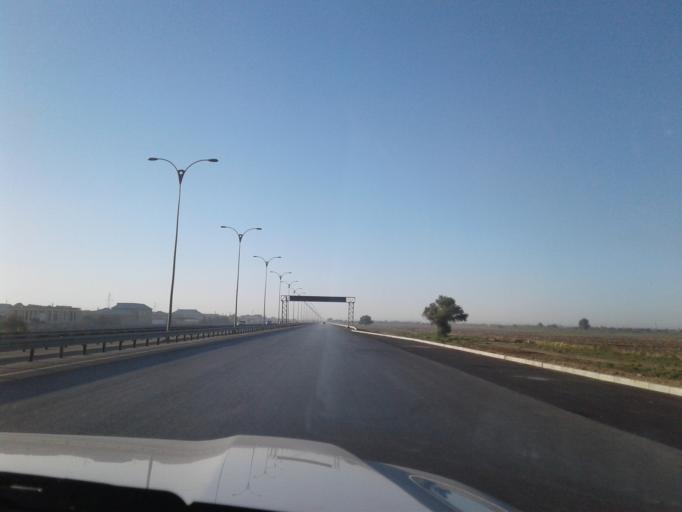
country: TM
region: Mary
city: Mary
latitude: 37.5687
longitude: 61.8373
